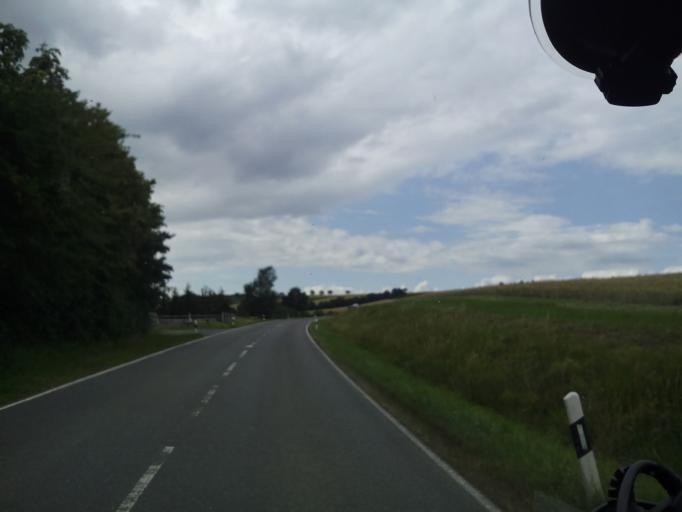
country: DE
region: Bavaria
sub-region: Upper Franconia
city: Sonnefeld
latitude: 50.2417
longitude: 11.1116
